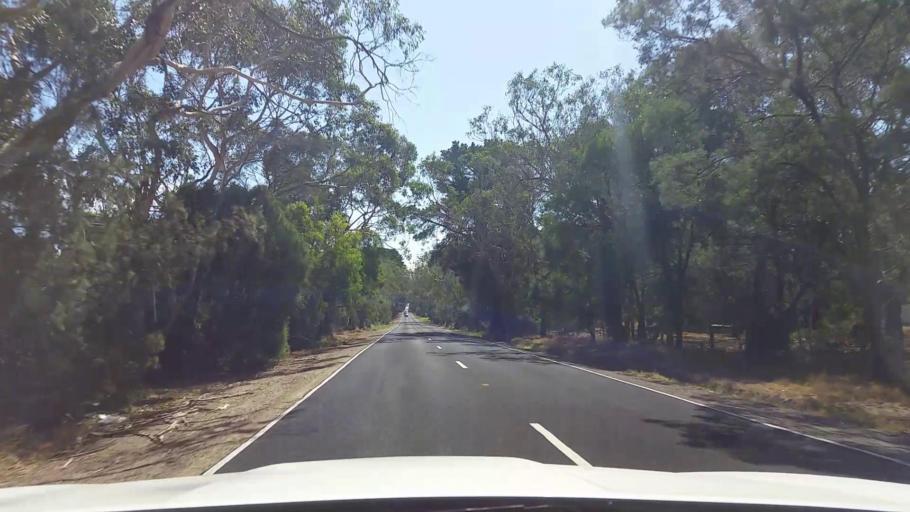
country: AU
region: Victoria
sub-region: Mornington Peninsula
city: Somerville
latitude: -38.2302
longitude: 145.1526
